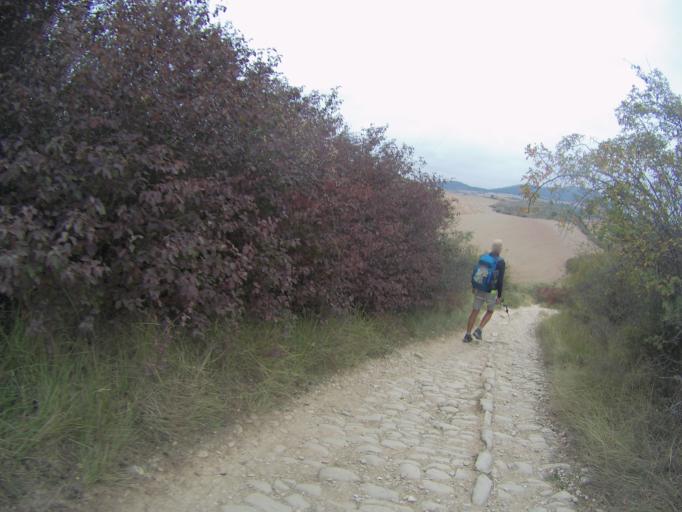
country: ES
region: Navarre
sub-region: Provincia de Navarra
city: Cirauqui
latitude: 42.6791
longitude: -1.9194
